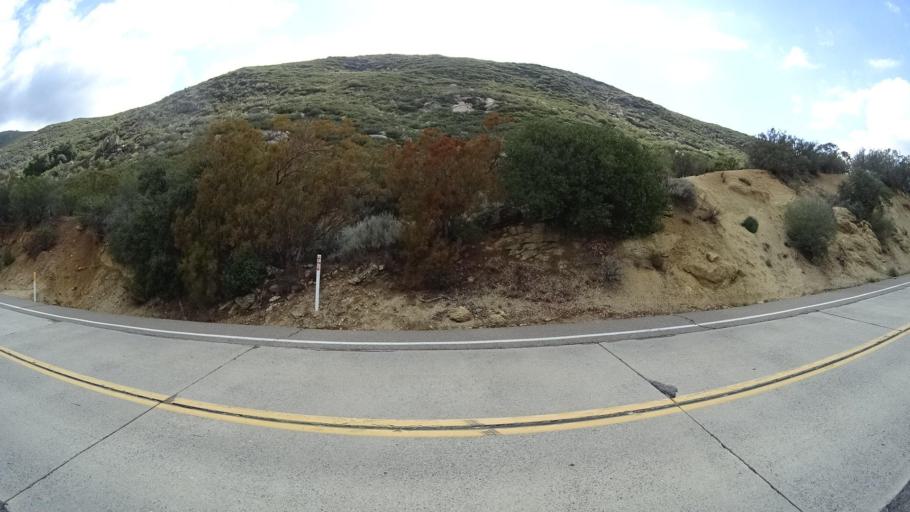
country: US
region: California
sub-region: San Diego County
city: Pine Valley
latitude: 32.8079
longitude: -116.5096
